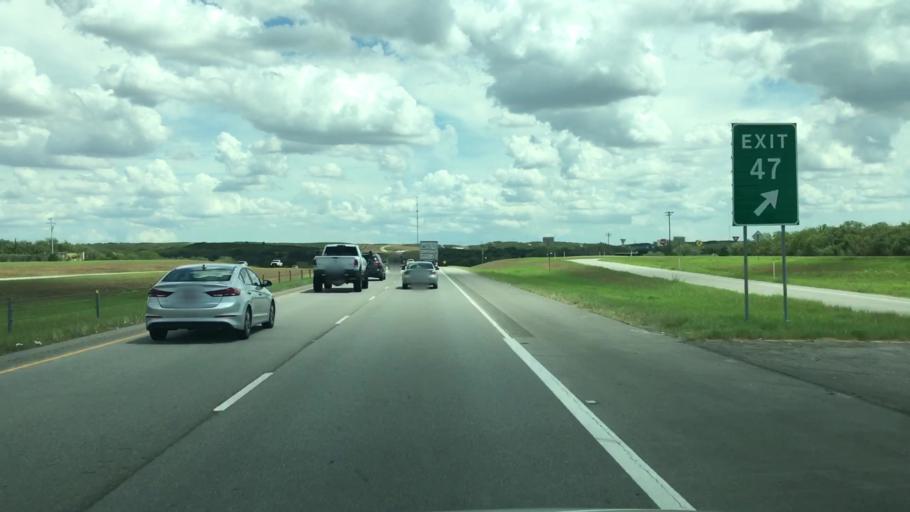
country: US
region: Texas
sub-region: Live Oak County
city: George West
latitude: 28.2653
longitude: -97.9368
